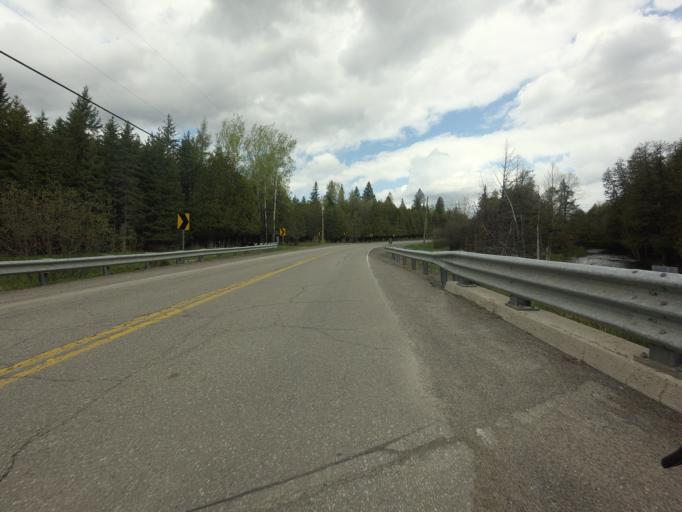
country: CA
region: Ontario
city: Carleton Place
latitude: 45.1801
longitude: -76.4008
